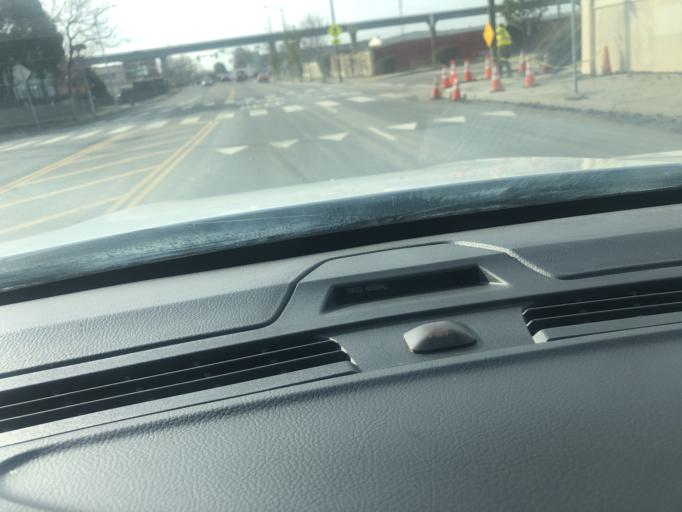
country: US
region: California
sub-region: Alameda County
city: San Leandro
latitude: 37.7404
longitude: -122.1784
